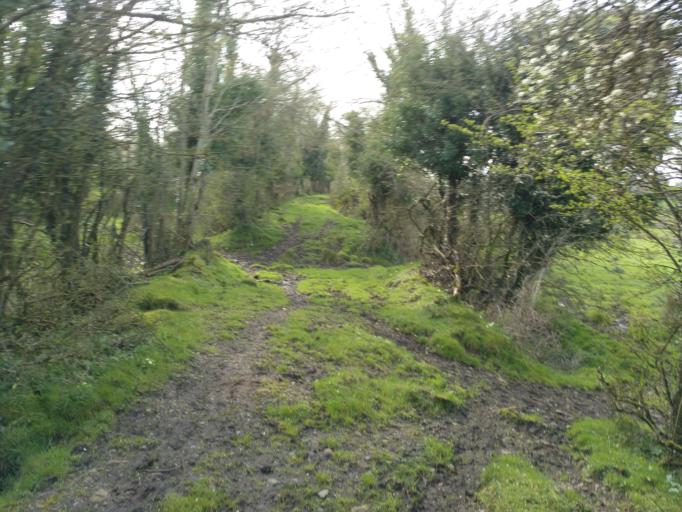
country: IE
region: Ulster
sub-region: County Monaghan
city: Clones
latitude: 54.1971
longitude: -7.1417
